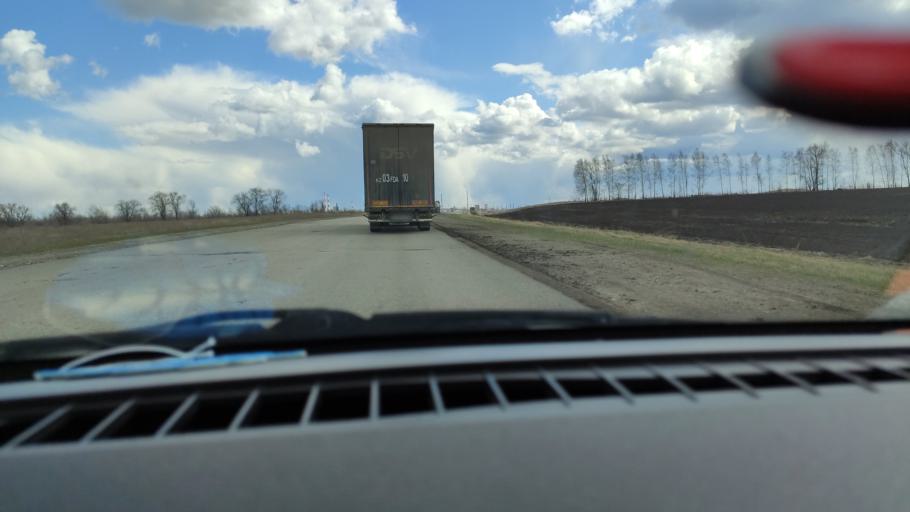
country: RU
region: Samara
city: Varlamovo
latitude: 53.1098
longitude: 48.3546
